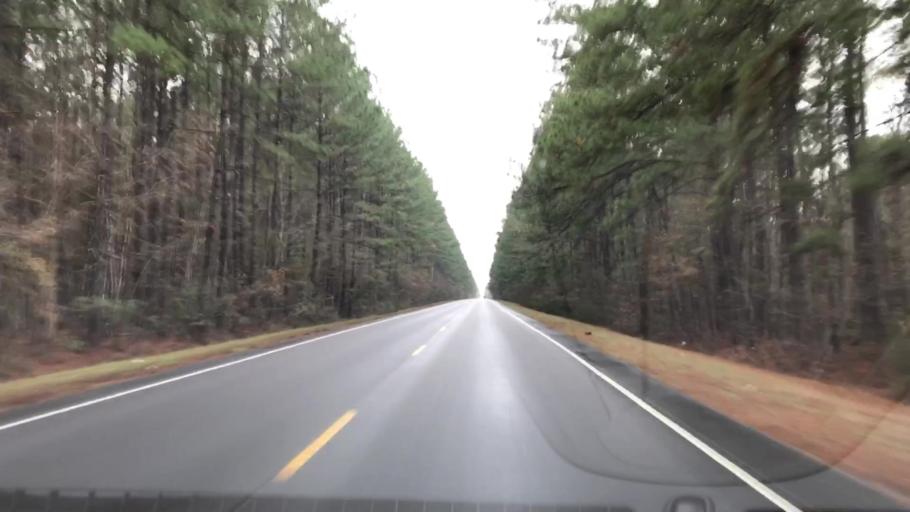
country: US
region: South Carolina
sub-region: Berkeley County
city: Saint Stephen
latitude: 33.2900
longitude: -79.7984
